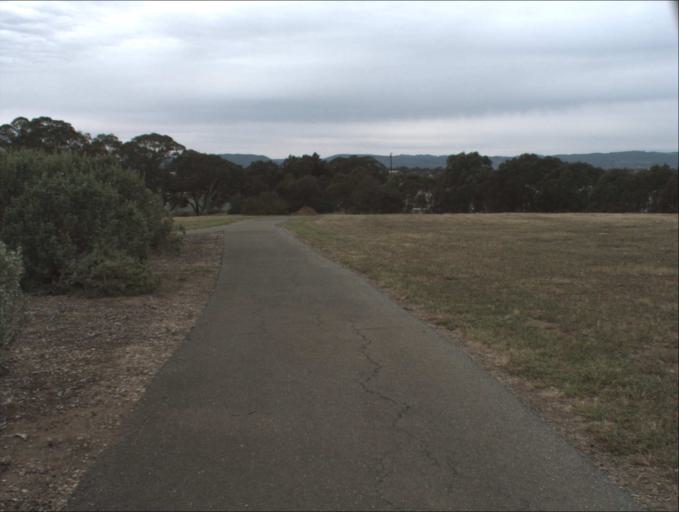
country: AU
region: South Australia
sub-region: Port Adelaide Enfield
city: Blair Athol
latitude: -34.8618
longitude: 138.5799
